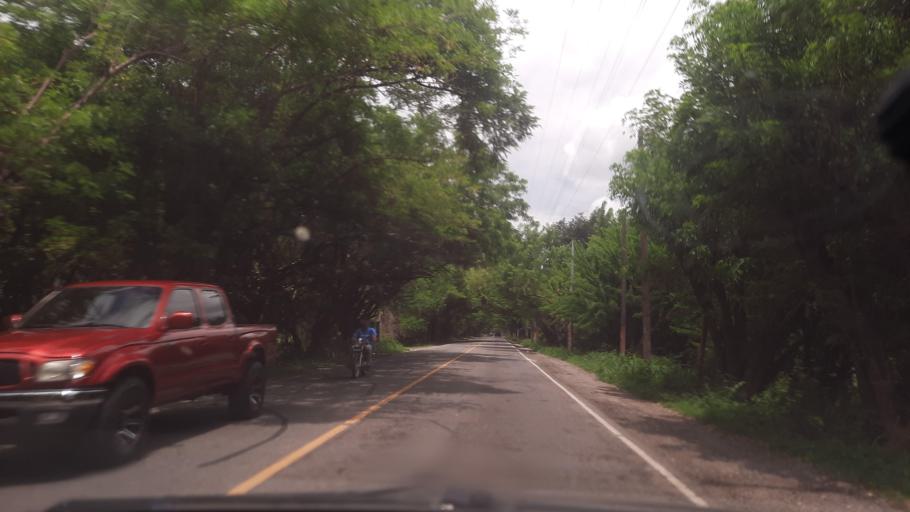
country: GT
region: Zacapa
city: Estanzuela
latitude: 14.9797
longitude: -89.5576
